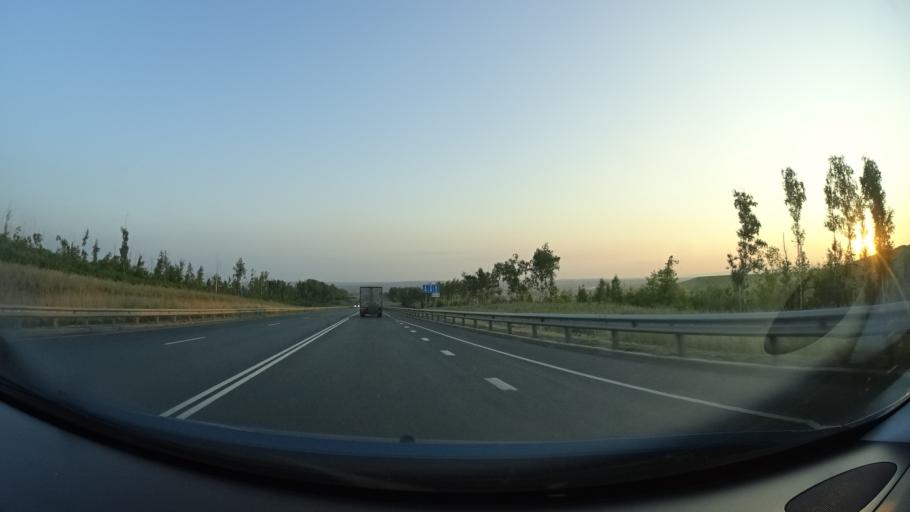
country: RU
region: Samara
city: Sernovodsk
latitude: 53.9092
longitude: 51.2929
